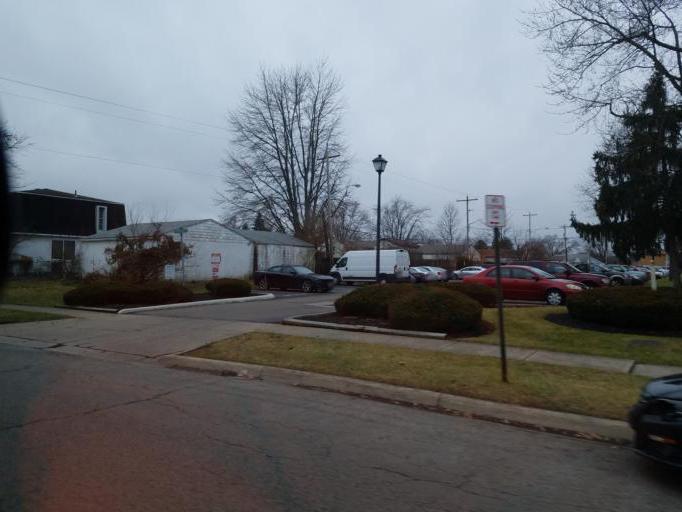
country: US
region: Ohio
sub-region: Franklin County
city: Minerva Park
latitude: 40.0844
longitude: -82.9698
